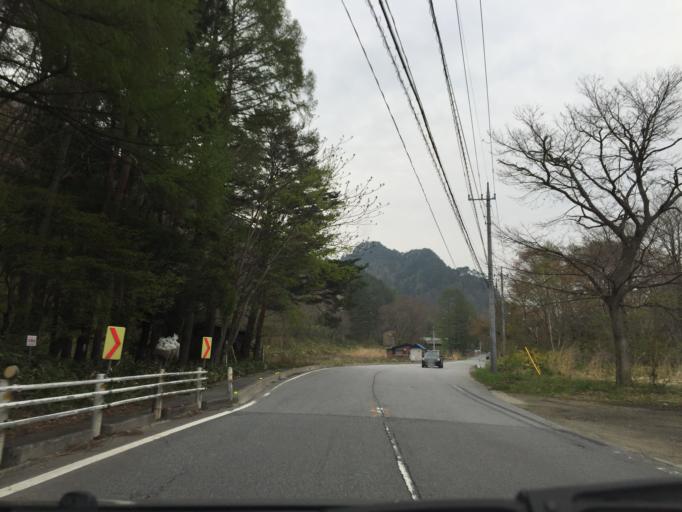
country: JP
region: Tochigi
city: Nikko
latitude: 37.0501
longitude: 139.7300
